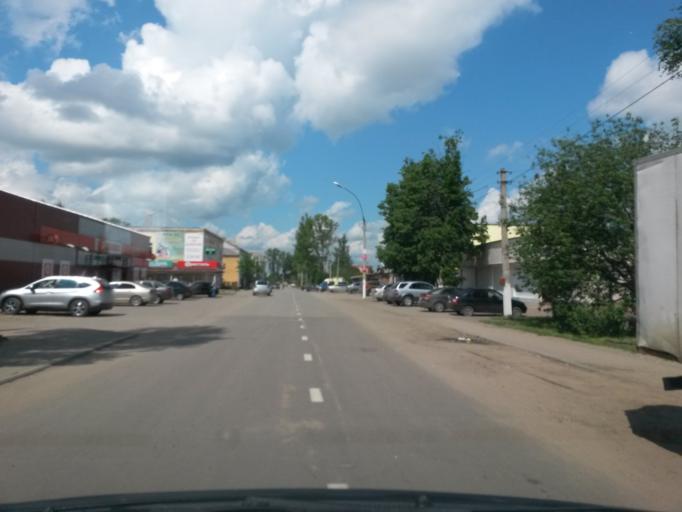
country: RU
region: Jaroslavl
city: Gavrilov-Yam
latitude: 57.3059
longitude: 39.8579
